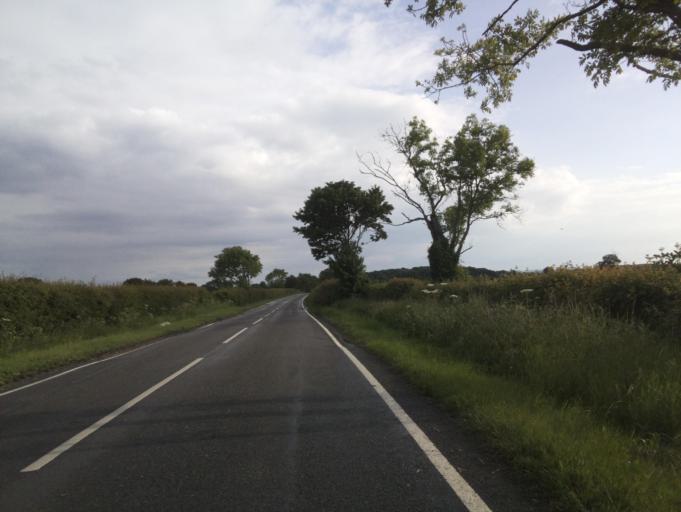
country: GB
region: England
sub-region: Lincolnshire
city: Great Gonerby
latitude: 53.0079
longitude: -0.6655
